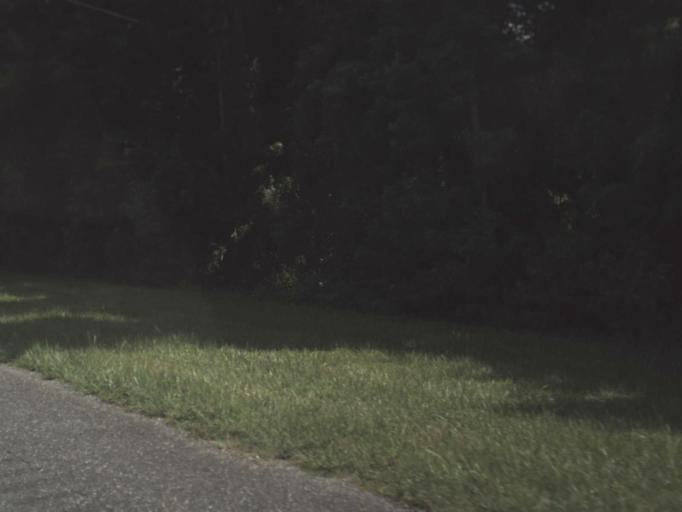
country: US
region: Florida
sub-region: Alachua County
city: Gainesville
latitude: 29.5262
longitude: -82.3070
